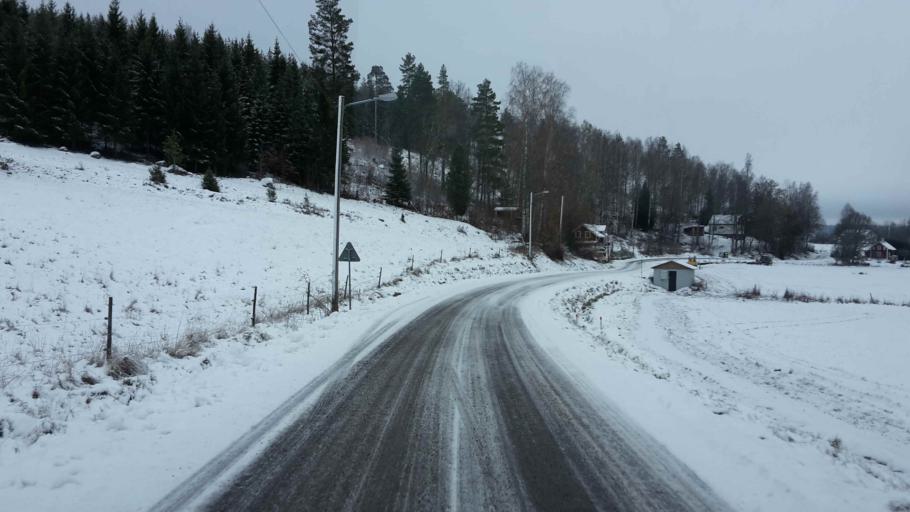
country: SE
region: Kalmar
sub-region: Vasterviks Kommun
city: Overum
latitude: 58.1574
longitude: 16.3306
